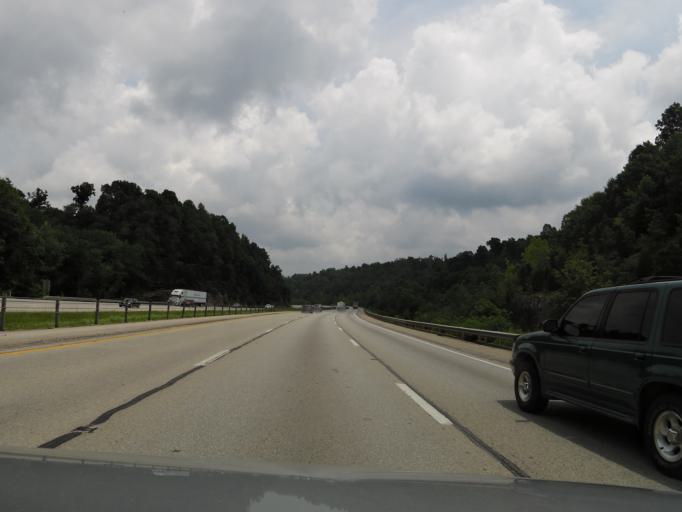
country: US
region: Kentucky
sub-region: Hardin County
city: Elizabethtown
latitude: 37.7399
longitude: -85.7997
